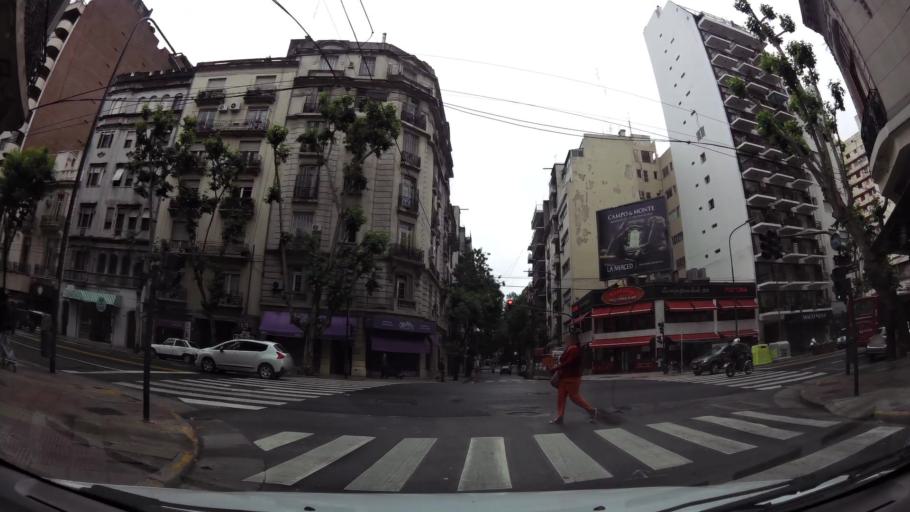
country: AR
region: Buenos Aires F.D.
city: Retiro
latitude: -34.5960
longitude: -58.4028
